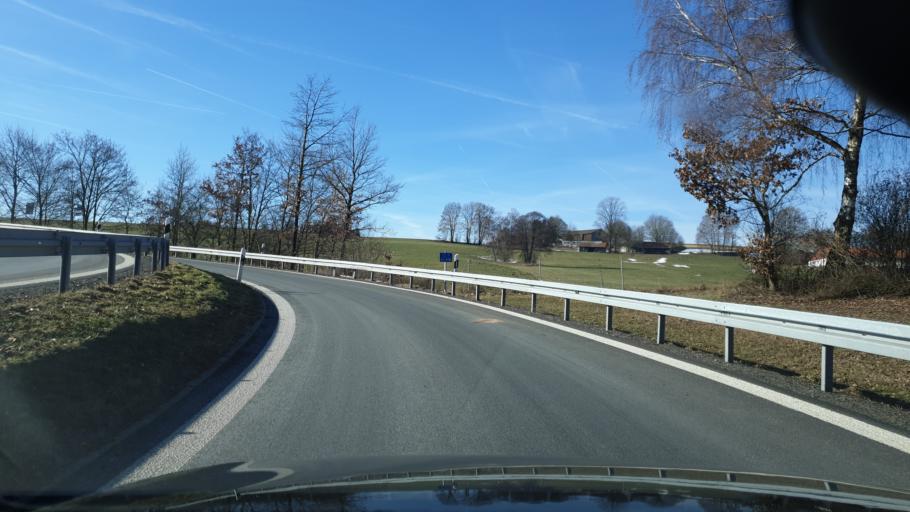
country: DE
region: Bavaria
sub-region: Upper Franconia
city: Marktschorgast
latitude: 50.0968
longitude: 11.6931
